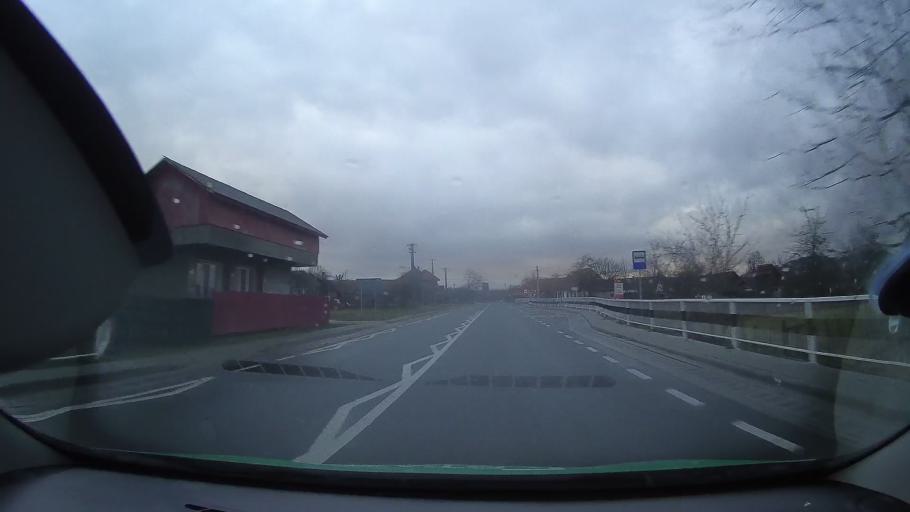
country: RO
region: Hunedoara
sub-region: Comuna Baia de Cris
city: Baia de Cris
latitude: 46.1720
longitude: 22.7145
